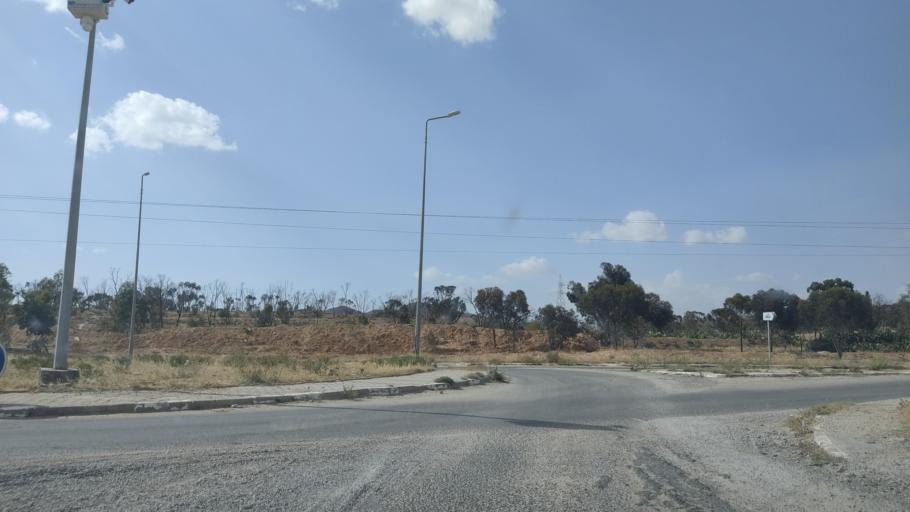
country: TN
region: Sidi Bu Zayd
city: Sidi Bouzid
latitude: 35.1093
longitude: 9.5424
